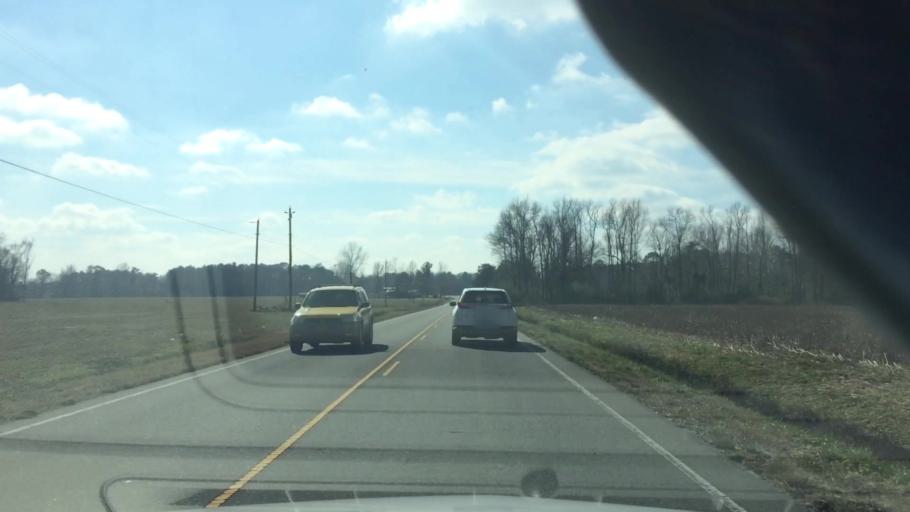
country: US
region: North Carolina
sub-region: Duplin County
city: Beulaville
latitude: 34.8858
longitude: -77.7857
